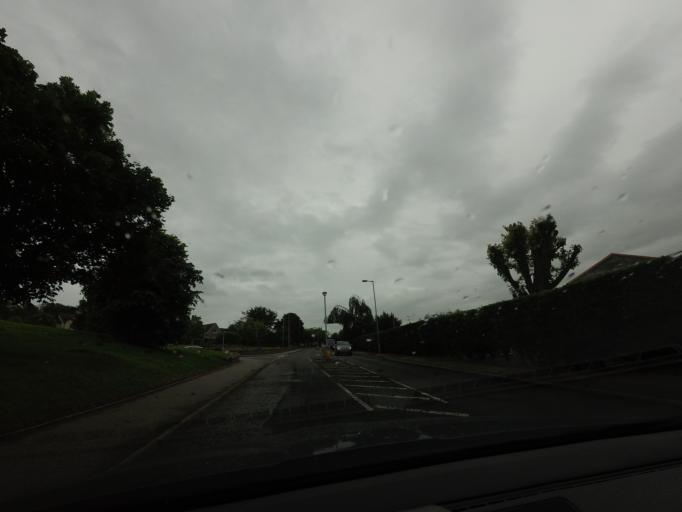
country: GB
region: Scotland
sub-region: Aberdeenshire
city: Turriff
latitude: 57.5423
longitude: -2.4752
